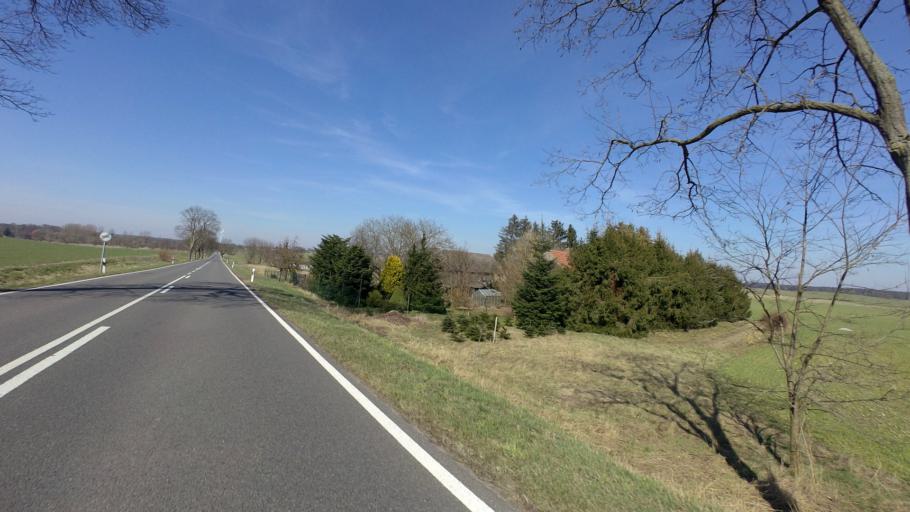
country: DE
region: Brandenburg
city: Protzel
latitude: 52.6175
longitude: 14.0190
